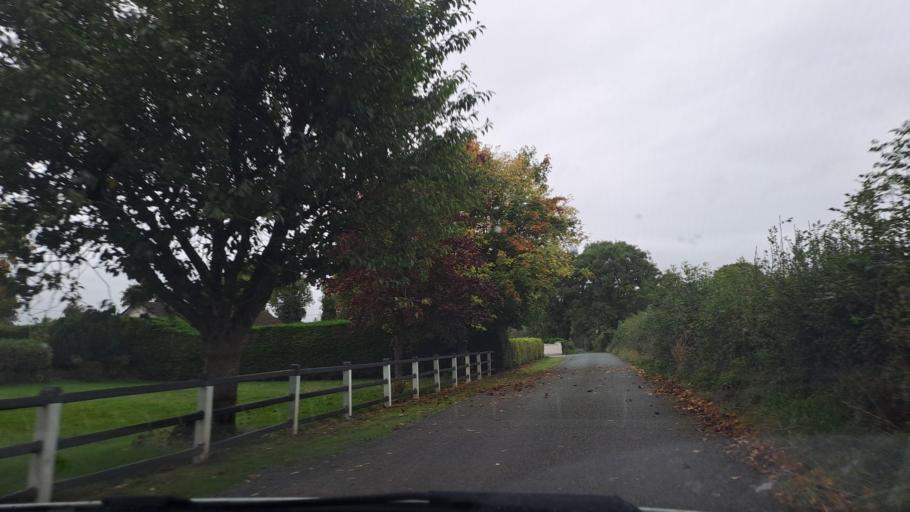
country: IE
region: Ulster
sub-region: County Monaghan
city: Carrickmacross
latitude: 53.9827
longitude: -6.7552
